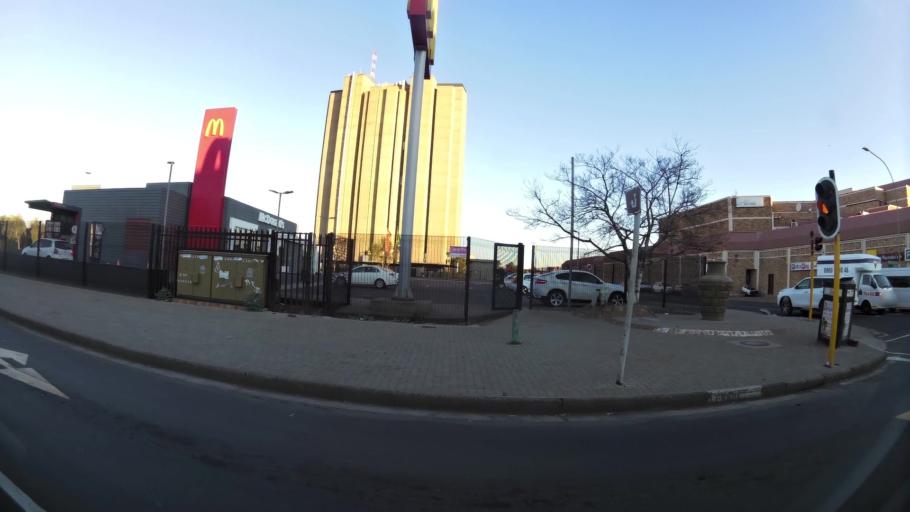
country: ZA
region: Northern Cape
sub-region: Frances Baard District Municipality
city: Kimberley
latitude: -28.7430
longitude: 24.7652
